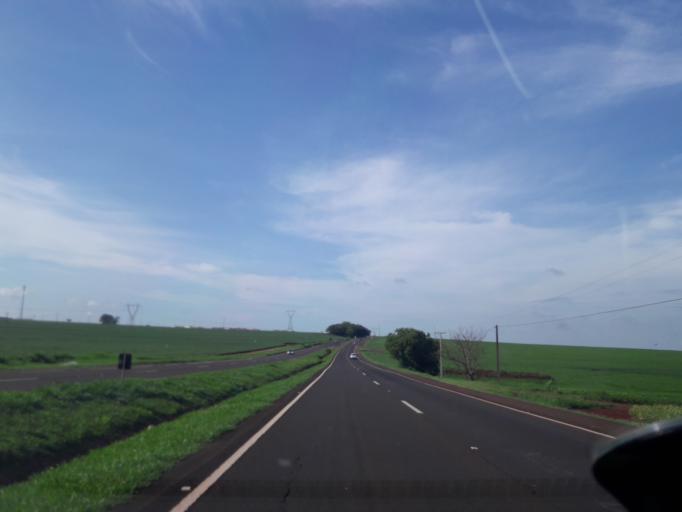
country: BR
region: Parana
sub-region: Paicandu
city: Paicandu
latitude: -23.5932
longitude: -52.0764
